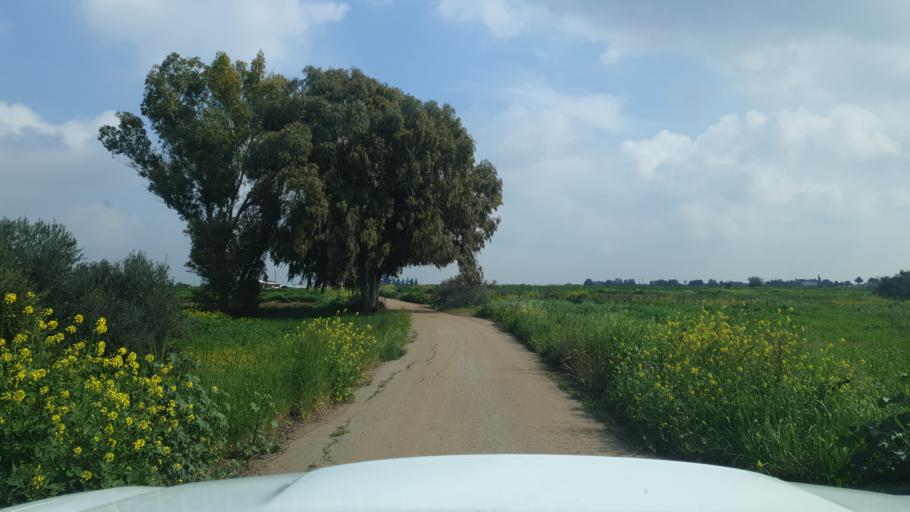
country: CY
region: Lefkosia
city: Kato Deftera
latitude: 35.0872
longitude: 33.2921
